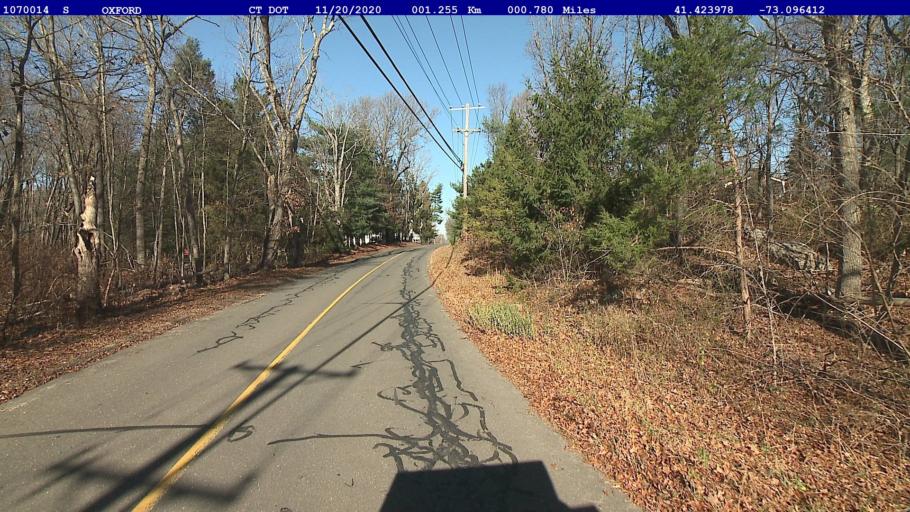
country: US
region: Connecticut
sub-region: New Haven County
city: Oxford
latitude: 41.4240
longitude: -73.0964
